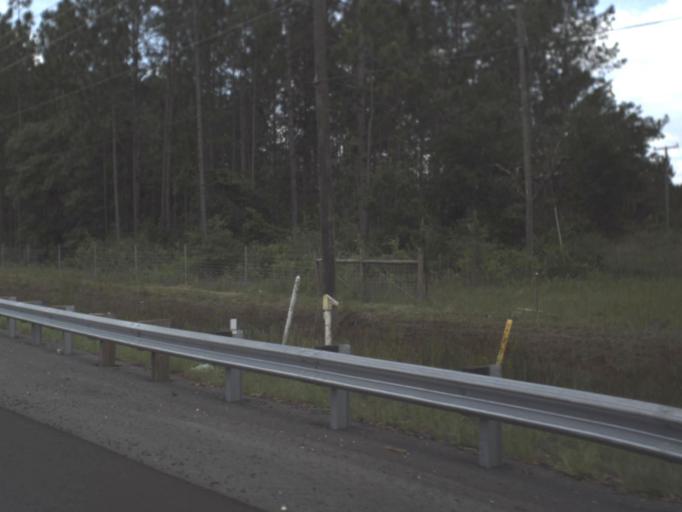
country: US
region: Florida
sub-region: Duval County
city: Baldwin
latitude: 30.4218
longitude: -81.9270
